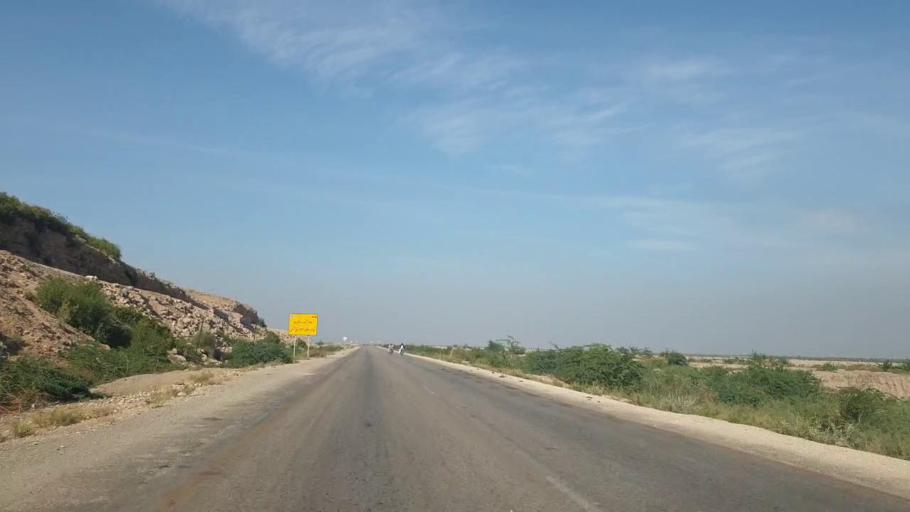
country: PK
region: Sindh
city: Sehwan
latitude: 26.3672
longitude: 67.8738
